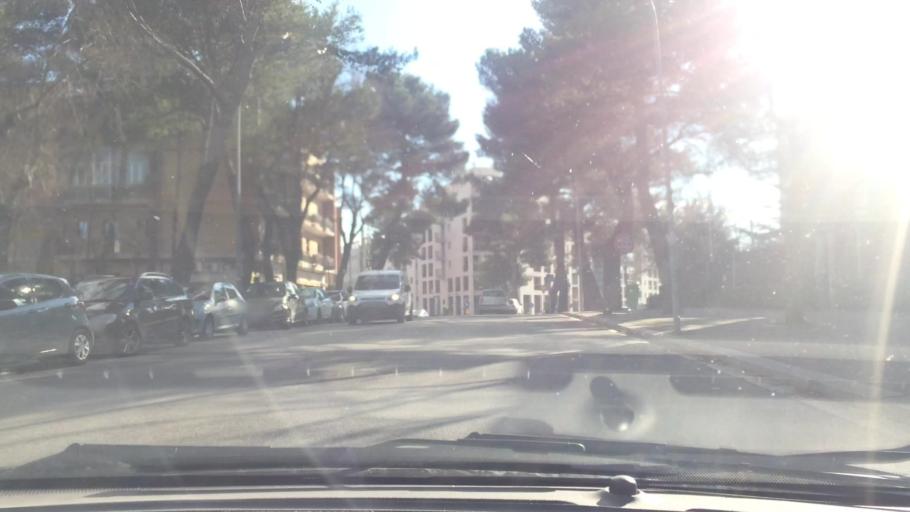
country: IT
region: Basilicate
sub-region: Provincia di Matera
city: Matera
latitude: 40.6697
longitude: 16.5983
